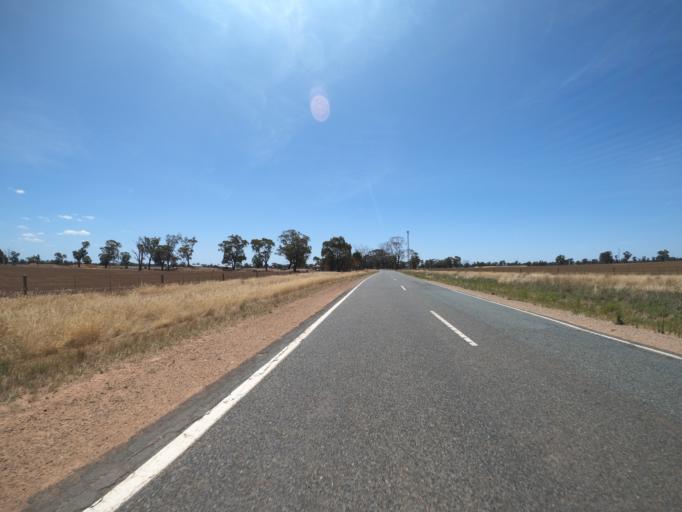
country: AU
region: Victoria
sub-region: Moira
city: Yarrawonga
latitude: -36.1911
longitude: 145.9671
